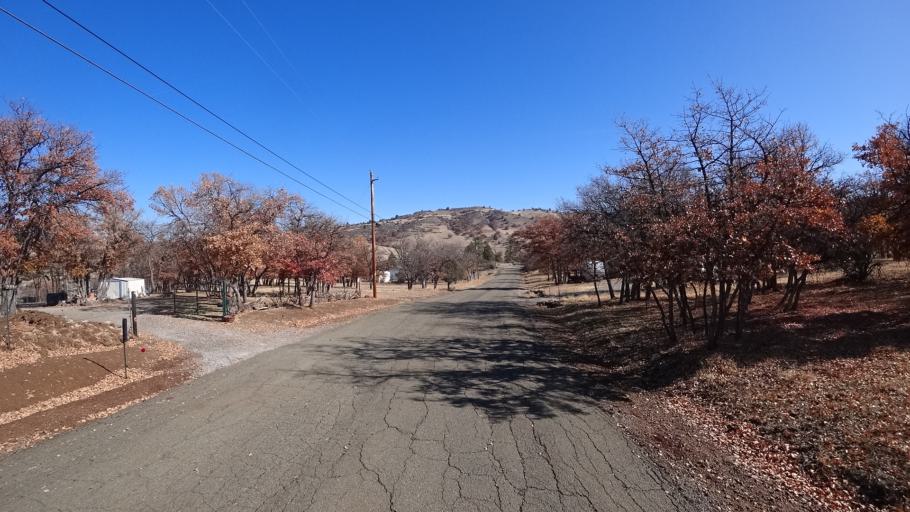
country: US
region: California
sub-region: Siskiyou County
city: Montague
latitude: 41.8870
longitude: -122.4865
